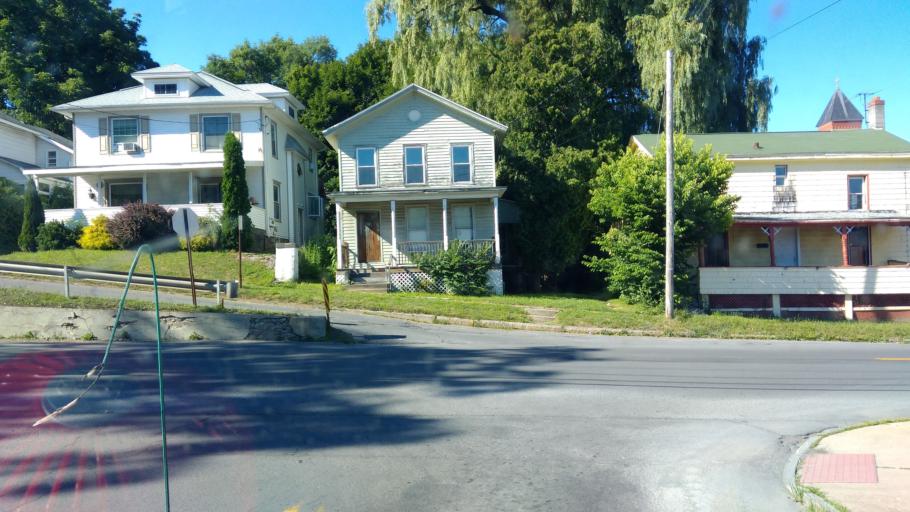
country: US
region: New York
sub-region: Wayne County
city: Lyons
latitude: 43.0628
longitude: -76.9960
